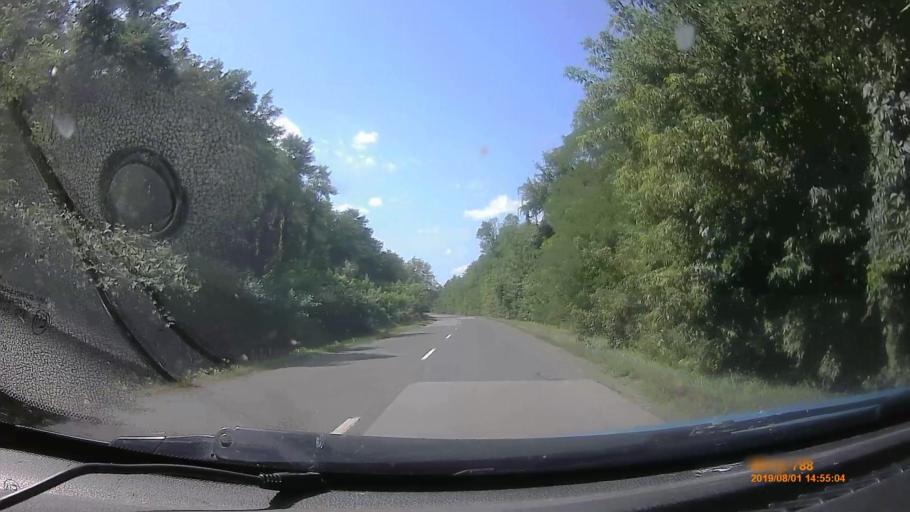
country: HU
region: Baranya
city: Vajszlo
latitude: 45.8683
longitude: 17.9616
